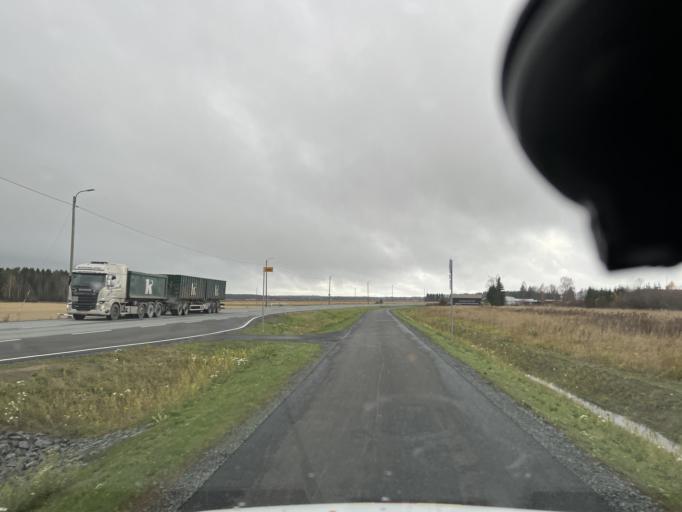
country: FI
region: Northern Ostrobothnia
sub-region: Ylivieska
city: Sievi
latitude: 63.9483
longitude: 24.5208
